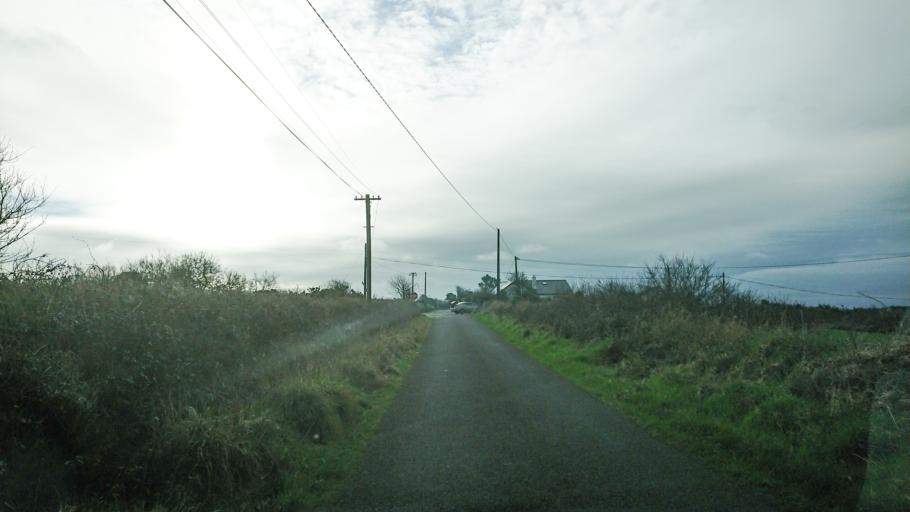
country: IE
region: Munster
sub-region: Waterford
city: Tra Mhor
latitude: 52.1448
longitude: -7.1938
